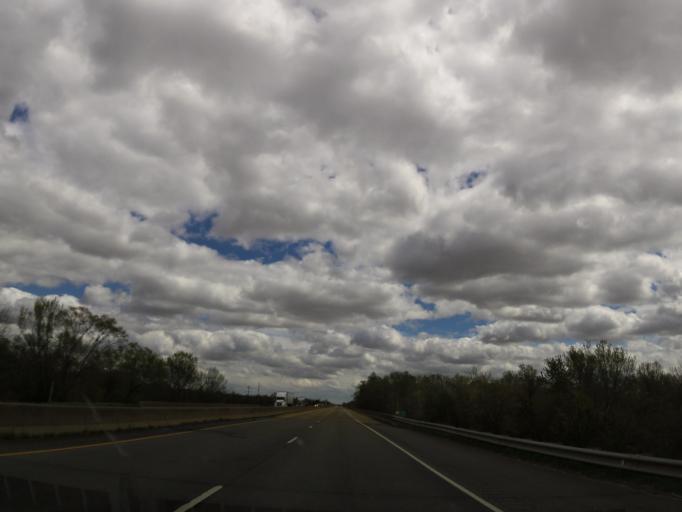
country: US
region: Arkansas
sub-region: Poinsett County
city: Marked Tree
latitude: 35.5391
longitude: -90.4897
